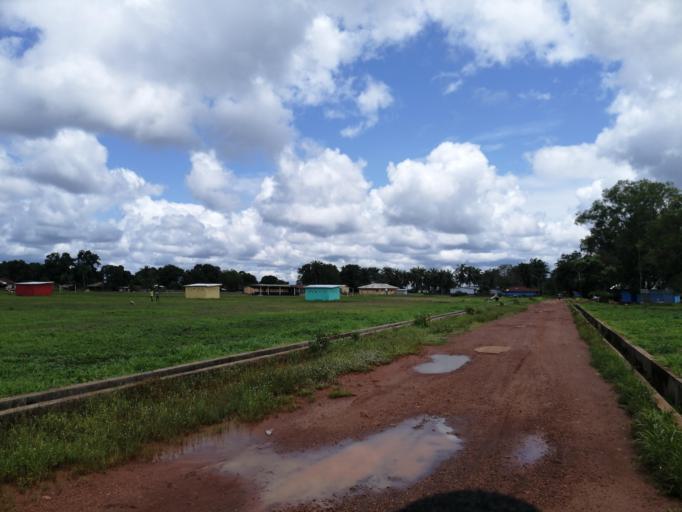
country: SL
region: Northern Province
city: Port Loko
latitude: 8.7769
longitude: -12.7906
